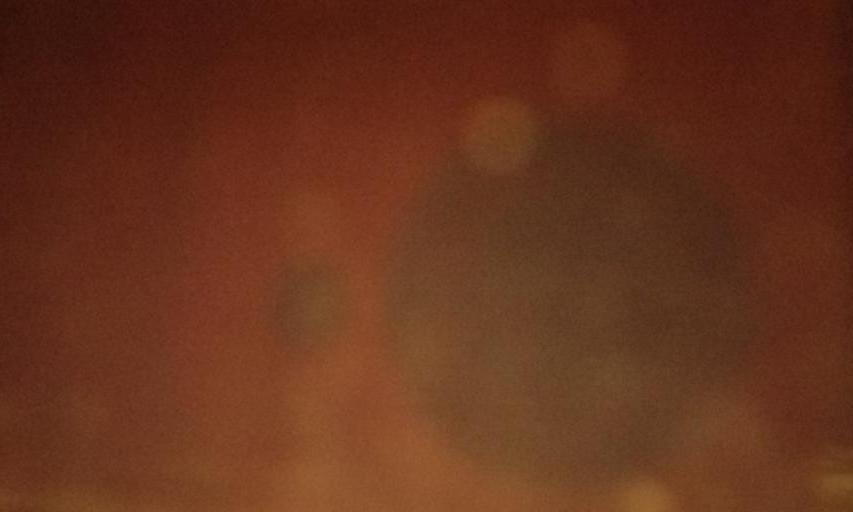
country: JP
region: Hiroshima
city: Onomichi
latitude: 34.4162
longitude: 133.1439
